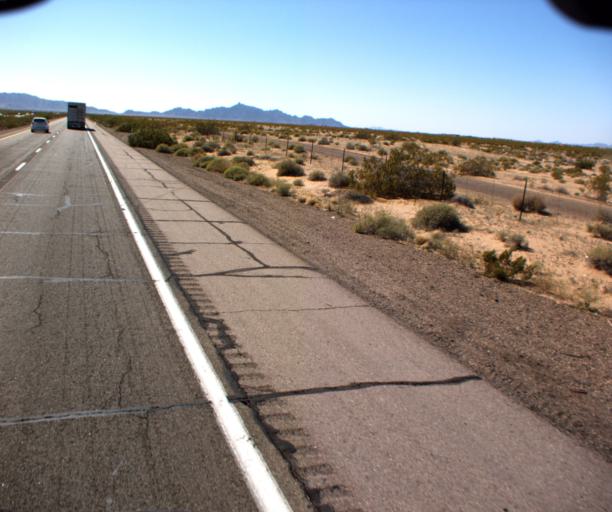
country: US
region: Arizona
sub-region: Yuma County
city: Wellton
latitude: 32.7765
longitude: -113.5947
